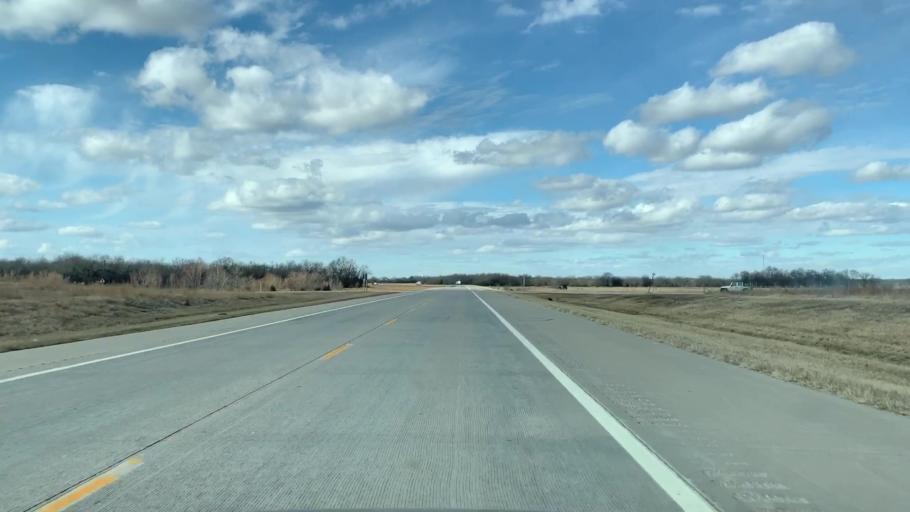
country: US
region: Kansas
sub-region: Labette County
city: Parsons
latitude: 37.3549
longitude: -95.2133
